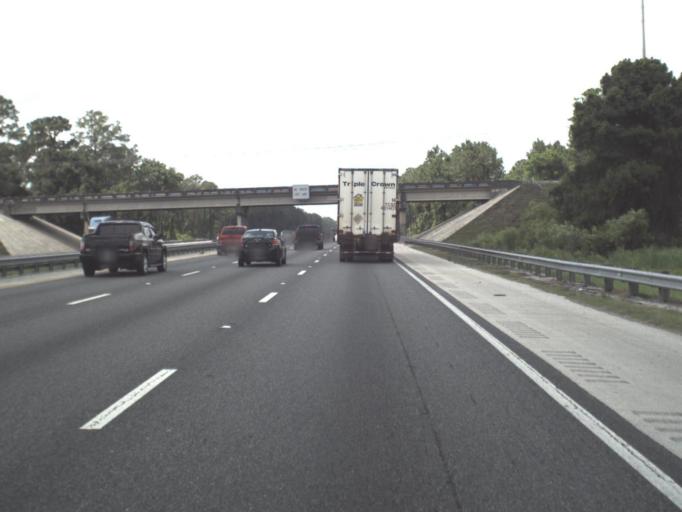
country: US
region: Florida
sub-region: Saint Johns County
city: Saint Augustine South
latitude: 29.8602
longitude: -81.3945
